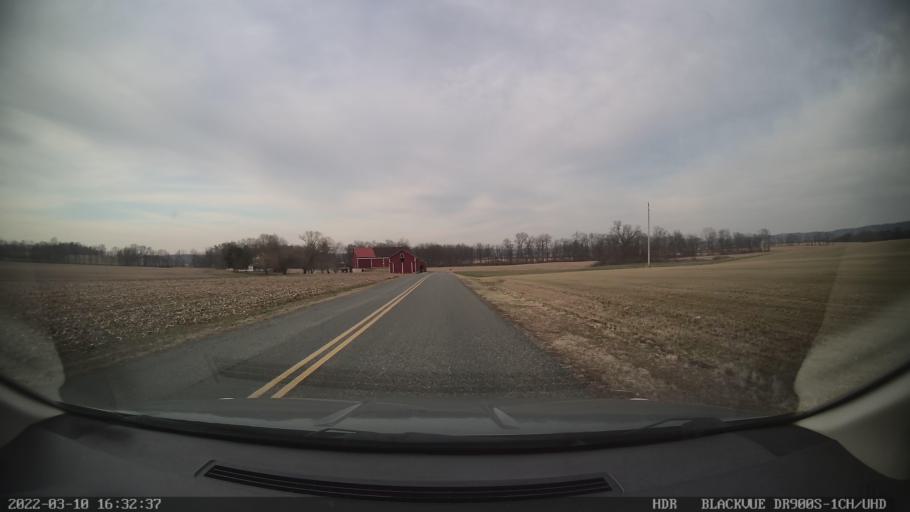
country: US
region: Pennsylvania
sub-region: Berks County
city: Oley
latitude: 40.3634
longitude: -75.7881
